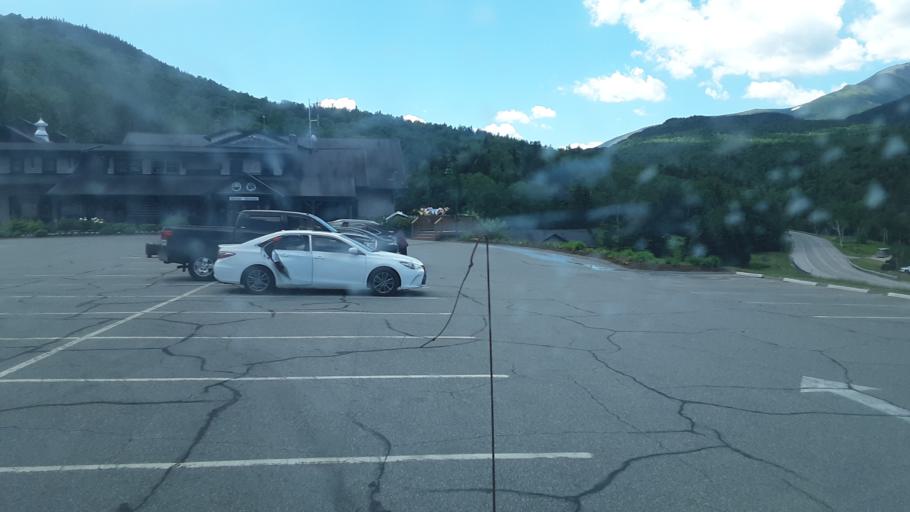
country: US
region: New Hampshire
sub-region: Coos County
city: Gorham
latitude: 44.2890
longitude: -71.2245
